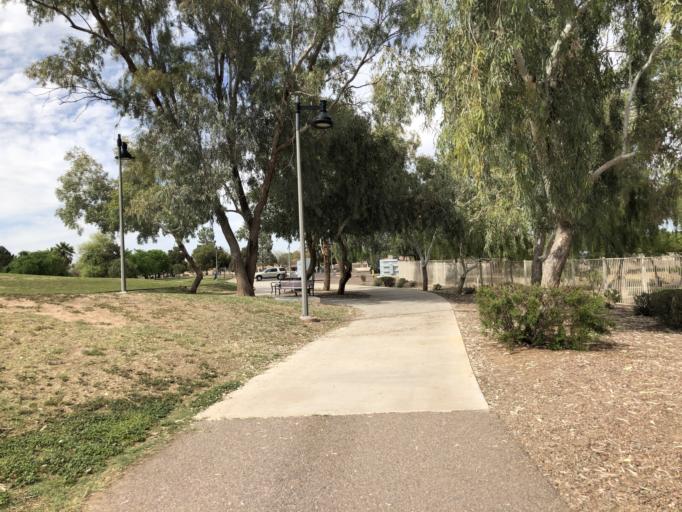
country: US
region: Arizona
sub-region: Maricopa County
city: Guadalupe
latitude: 33.3122
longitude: -111.9186
